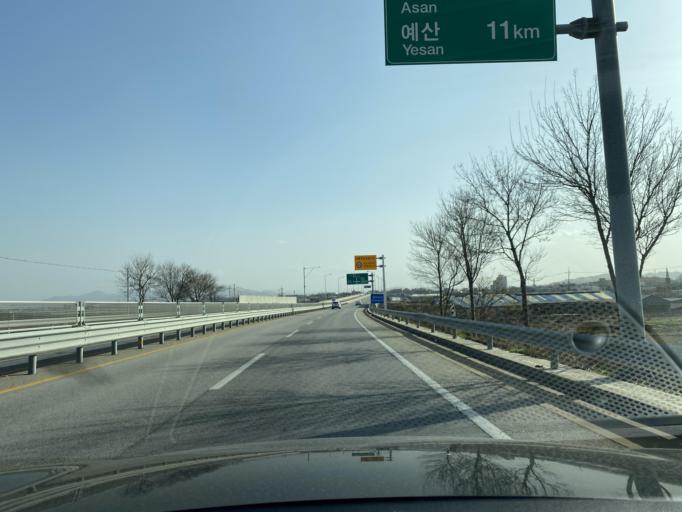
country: KR
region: Chungcheongnam-do
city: Yesan
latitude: 36.6924
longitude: 126.7320
